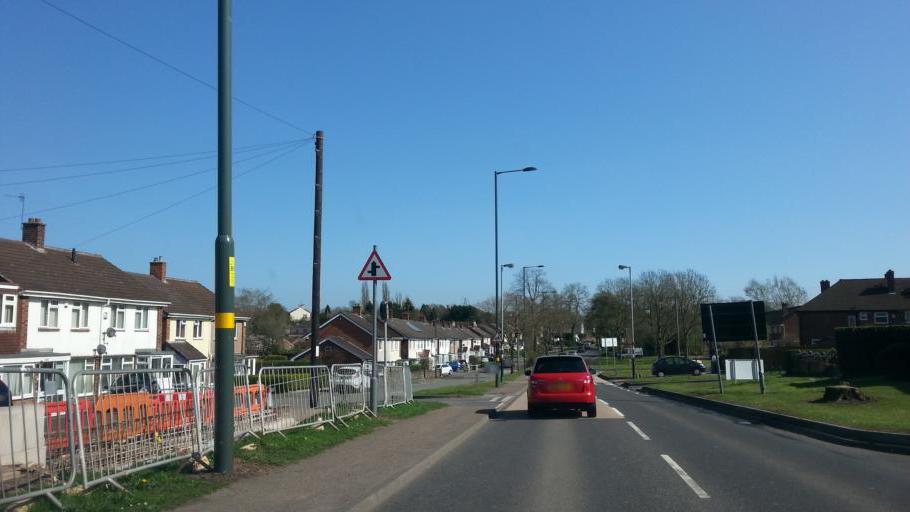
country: GB
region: England
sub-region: Worcestershire
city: Alvechurch
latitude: 52.3931
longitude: -1.9669
